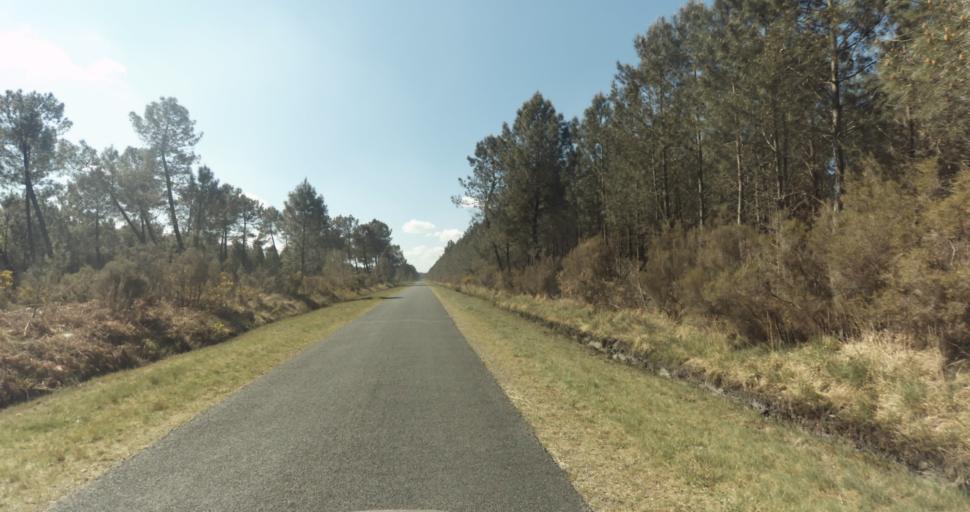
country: FR
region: Aquitaine
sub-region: Departement de la Gironde
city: Martignas-sur-Jalle
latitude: 44.7837
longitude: -0.8006
